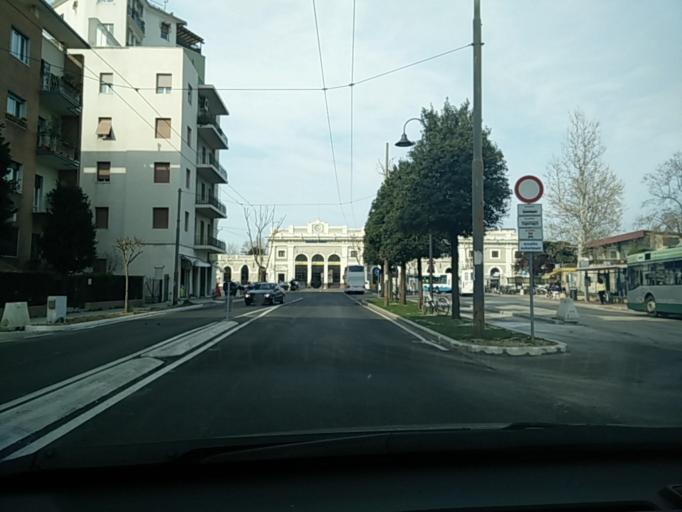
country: IT
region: Emilia-Romagna
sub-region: Provincia di Rimini
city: Rimini
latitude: 44.0630
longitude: 12.5731
